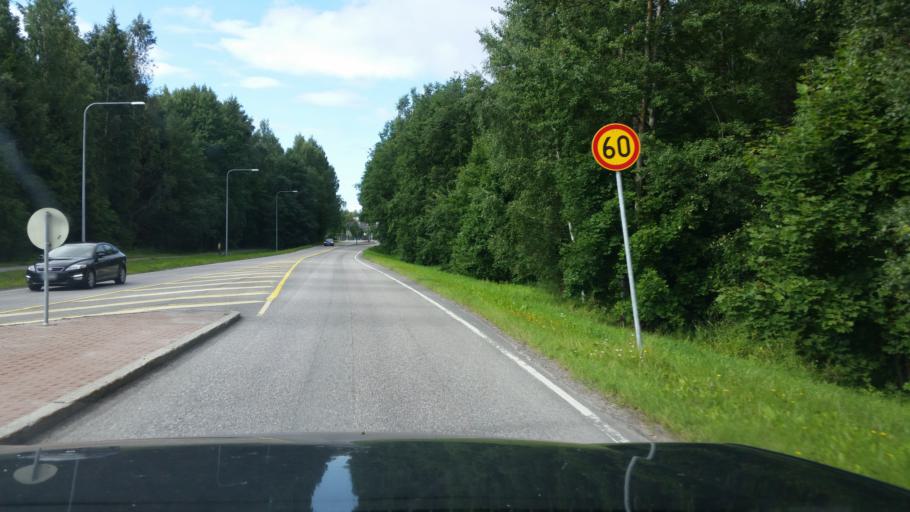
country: FI
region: Uusimaa
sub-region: Helsinki
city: Vantaa
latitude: 60.2232
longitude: 25.1136
